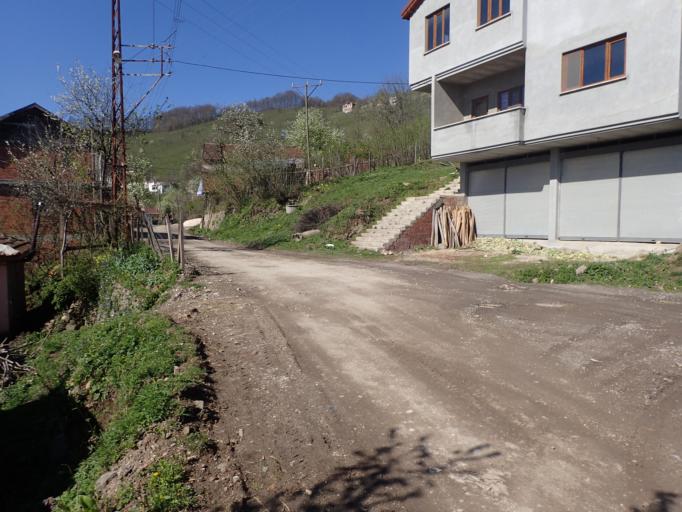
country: TR
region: Ordu
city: Korgan
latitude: 40.7633
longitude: 37.3085
